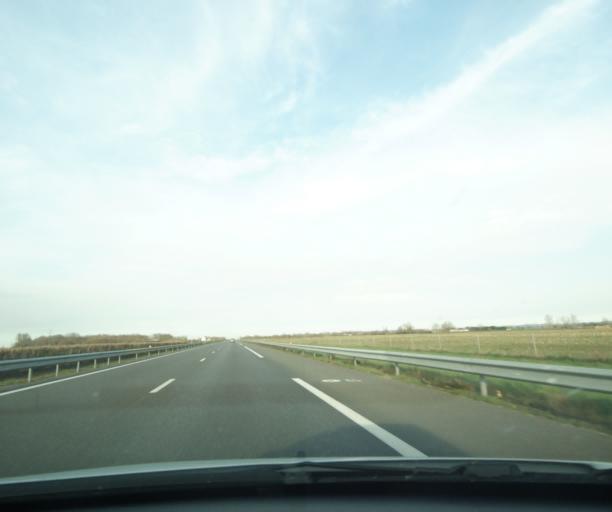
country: FR
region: Midi-Pyrenees
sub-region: Departement de la Haute-Garonne
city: Cazeres
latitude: 43.2489
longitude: 1.0959
